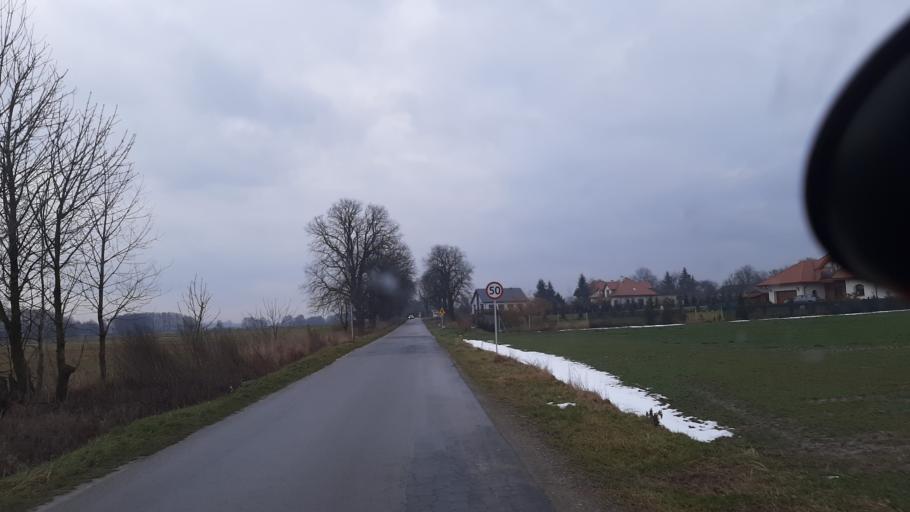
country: PL
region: Lublin Voivodeship
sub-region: Powiat lubelski
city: Jastkow
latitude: 51.3503
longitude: 22.5115
